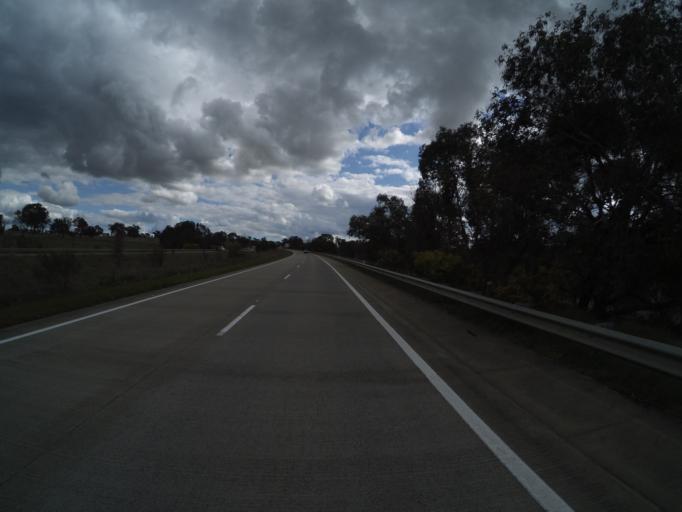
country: AU
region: New South Wales
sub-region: Yass Valley
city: Gundaroo
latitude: -34.7855
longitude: 149.2441
